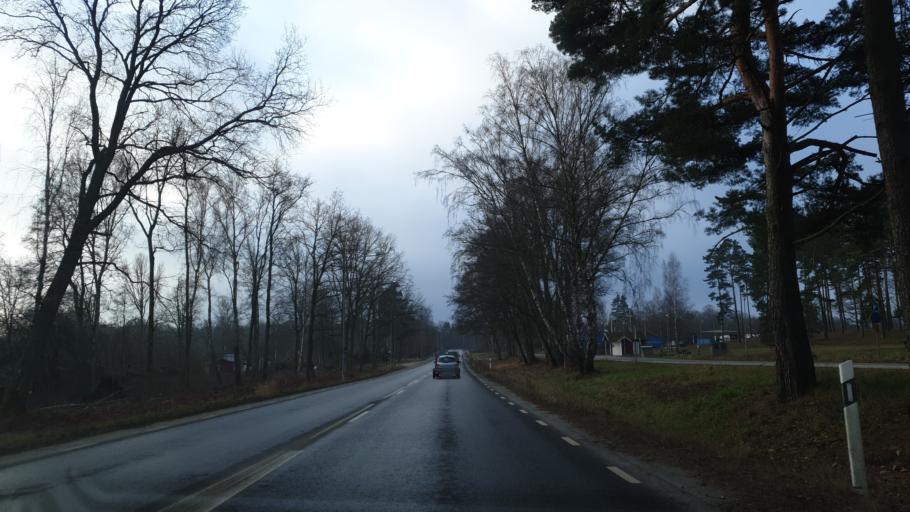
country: SE
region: Blekinge
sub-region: Karlshamns Kommun
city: Morrum
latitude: 56.1526
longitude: 14.6725
